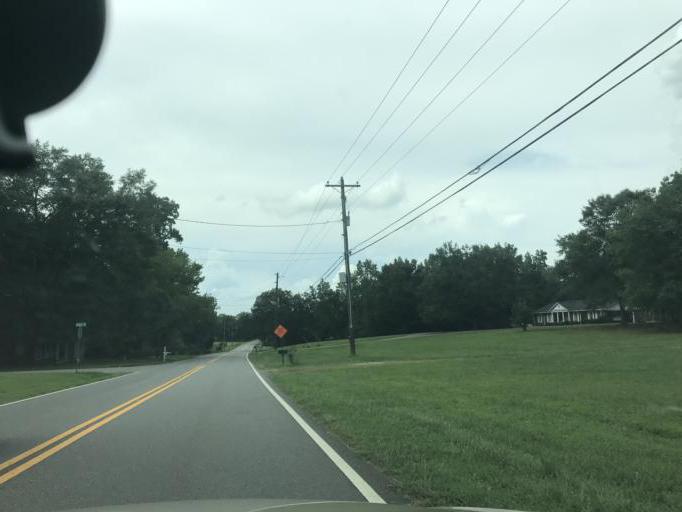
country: US
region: Georgia
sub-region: Forsyth County
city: Cumming
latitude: 34.2705
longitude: -84.2361
